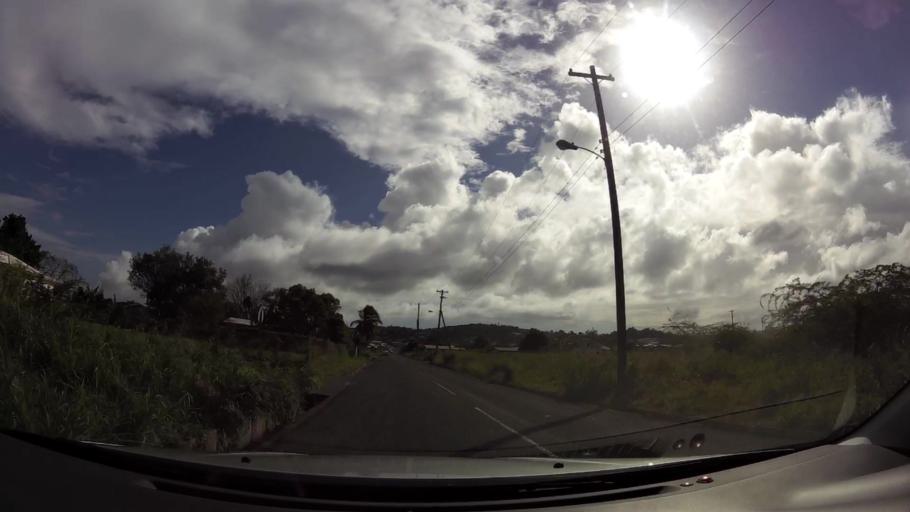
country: AG
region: Saint George
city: Piggotts
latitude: 17.1229
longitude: -61.8212
